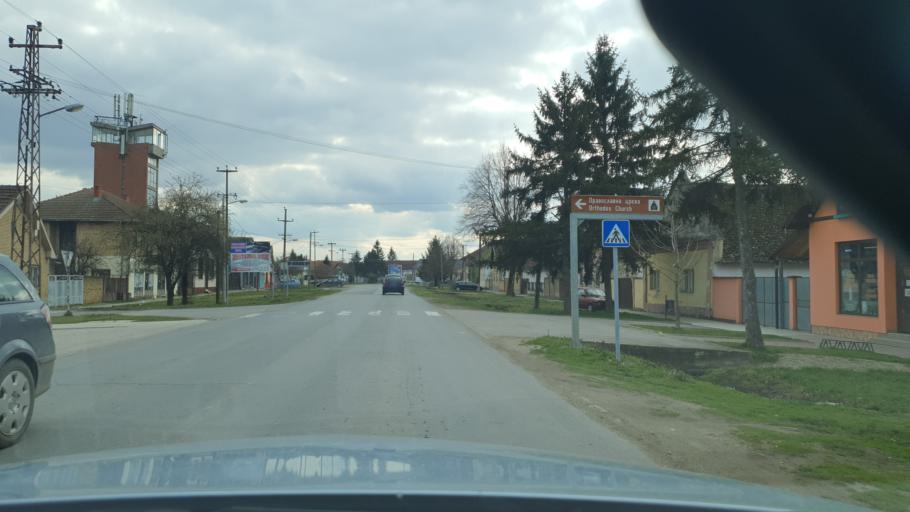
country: RS
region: Autonomna Pokrajina Vojvodina
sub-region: Juznobacki Okrug
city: Bac
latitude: 45.3936
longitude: 19.2372
